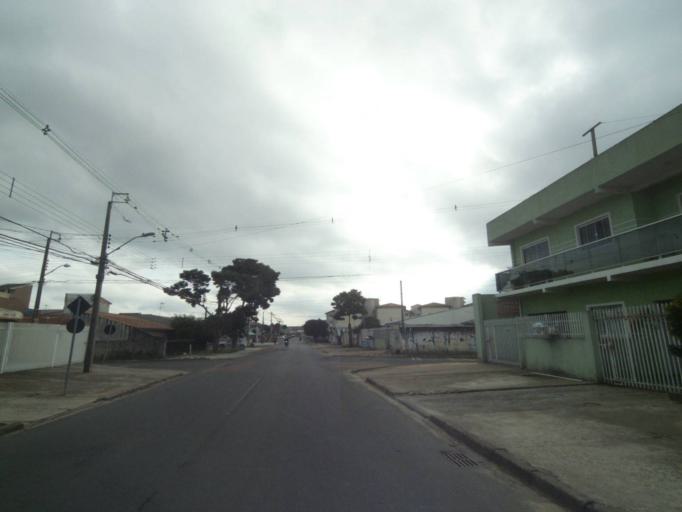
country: BR
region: Parana
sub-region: Sao Jose Dos Pinhais
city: Sao Jose dos Pinhais
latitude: -25.5439
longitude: -49.2491
